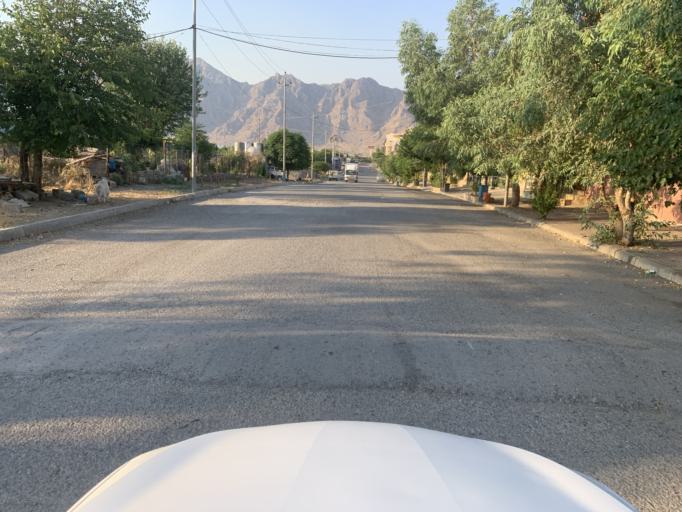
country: IQ
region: As Sulaymaniyah
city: Raniye
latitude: 36.2428
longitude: 44.8795
